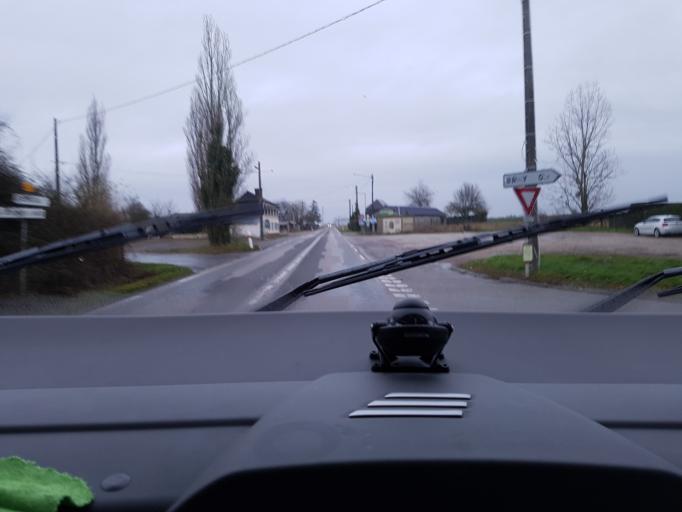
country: FR
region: Haute-Normandie
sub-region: Departement de l'Eure
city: Beaumont-le-Roger
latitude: 49.1118
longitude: 0.8436
